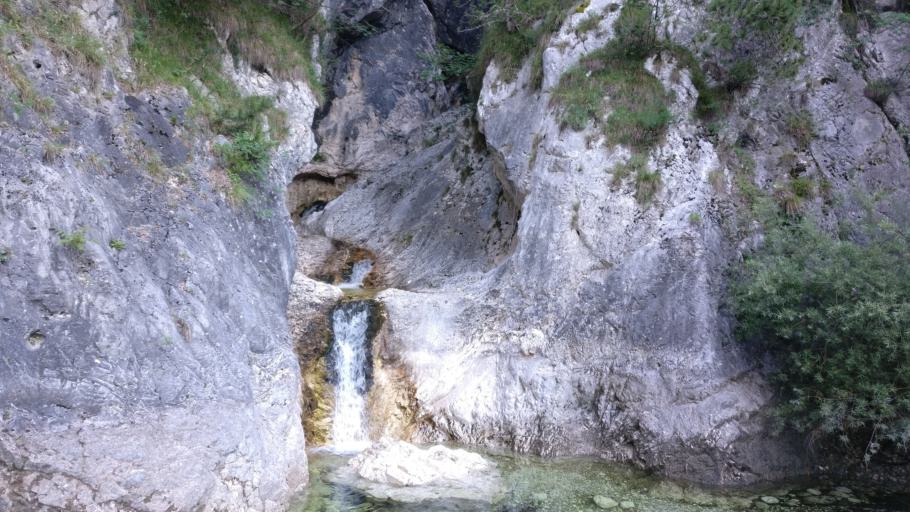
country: IT
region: Friuli Venezia Giulia
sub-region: Provincia di Udine
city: Amaro
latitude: 46.3850
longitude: 13.1201
